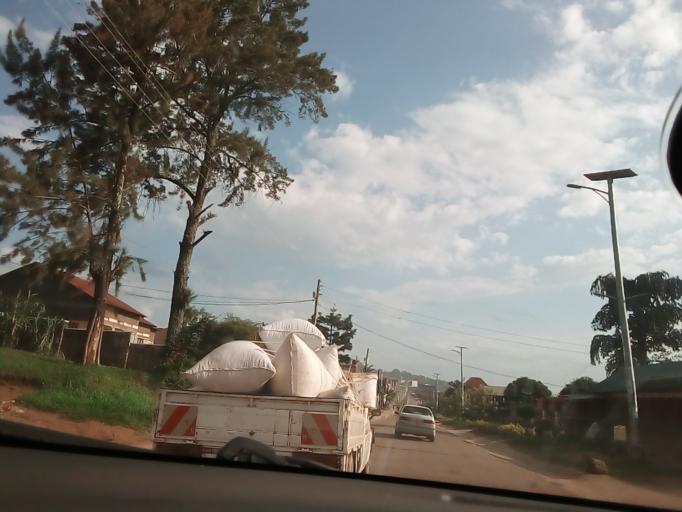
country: UG
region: Central Region
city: Masaka
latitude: -0.3493
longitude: 31.7421
